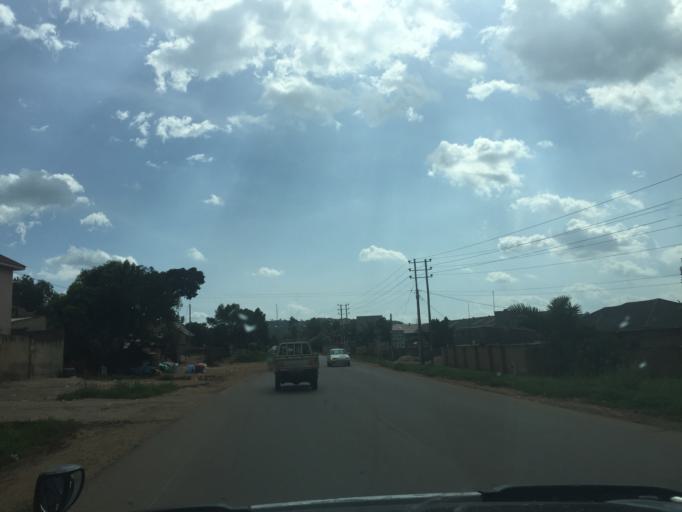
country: UG
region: Central Region
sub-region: Wakiso District
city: Wakiso
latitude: 0.5364
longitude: 32.5315
